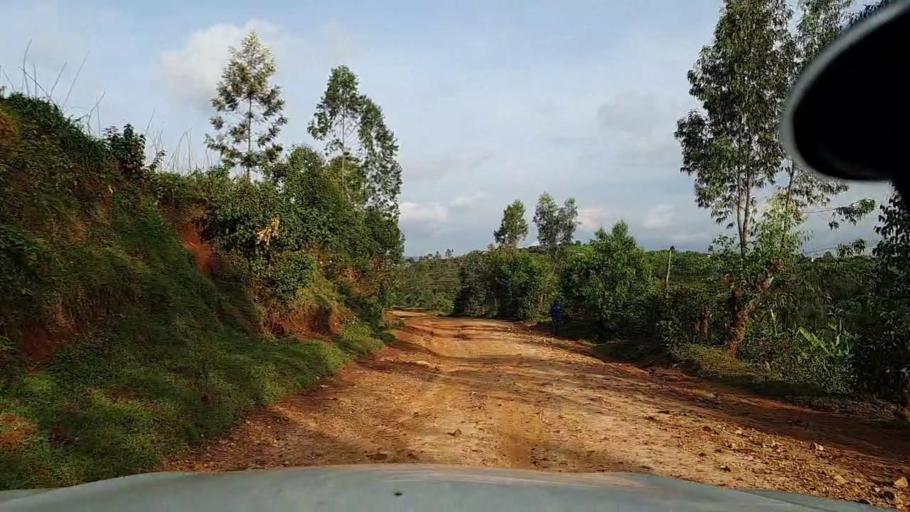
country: RW
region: Southern Province
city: Gitarama
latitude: -2.1860
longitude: 29.5655
